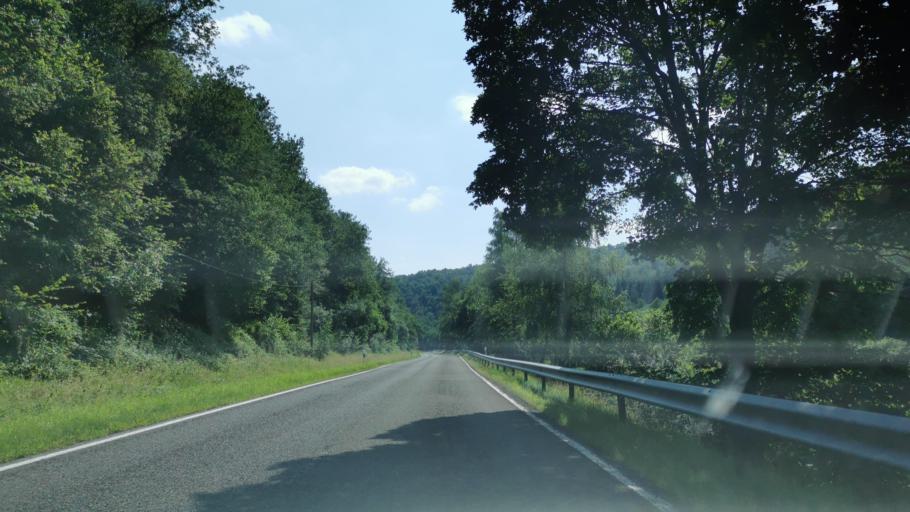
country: DE
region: Rheinland-Pfalz
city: Rorodt
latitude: 49.7775
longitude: 7.0481
